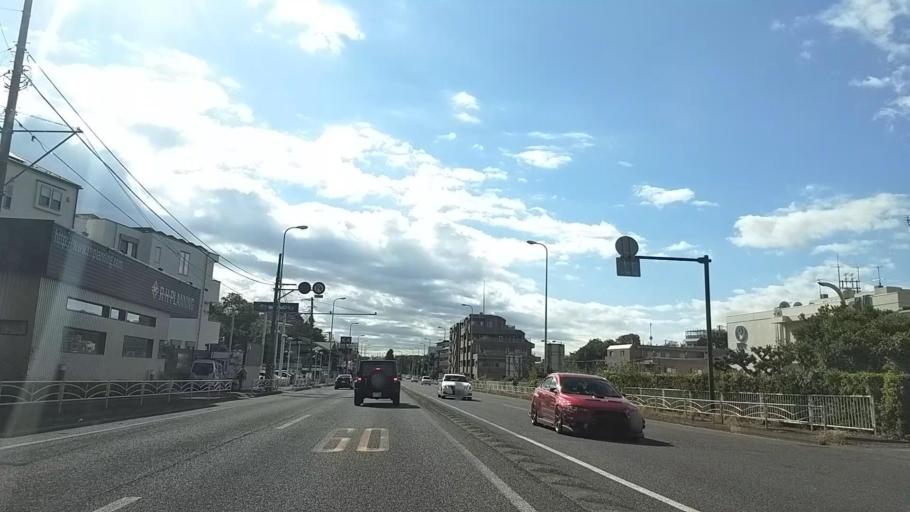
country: JP
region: Kanagawa
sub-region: Kawasaki-shi
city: Kawasaki
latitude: 35.5109
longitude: 139.6628
